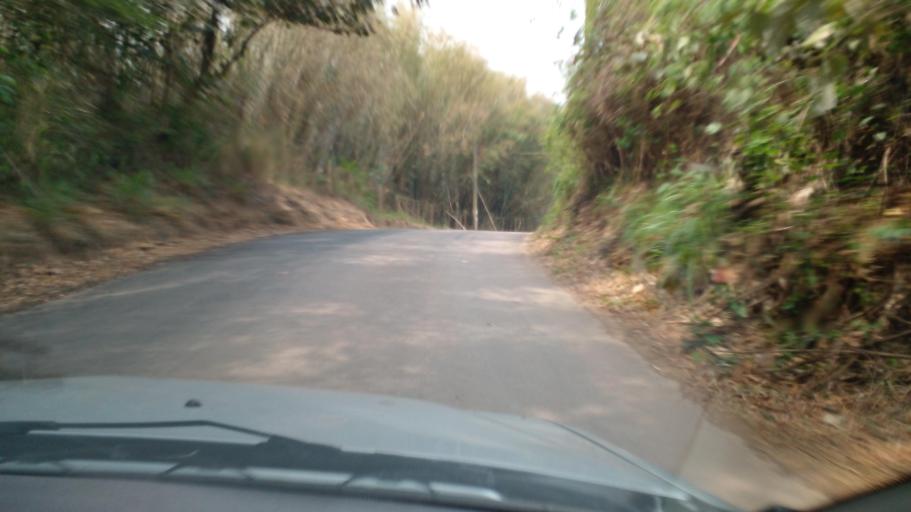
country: BR
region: Sao Paulo
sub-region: Jundiai
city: Jundiai
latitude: -23.1328
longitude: -46.8866
